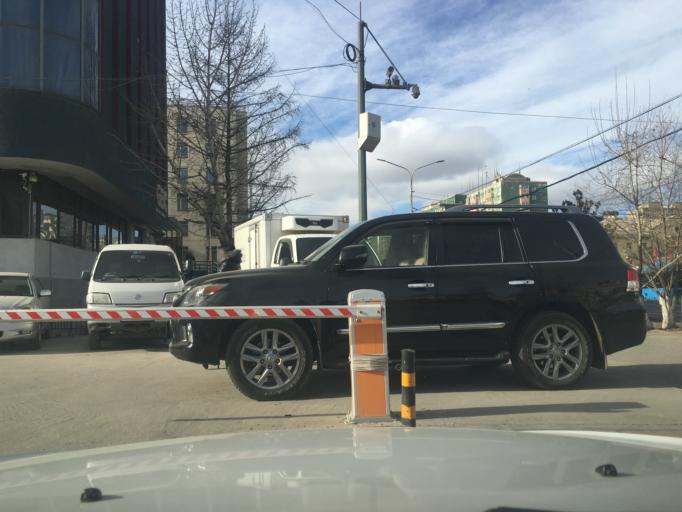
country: MN
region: Ulaanbaatar
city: Ulaanbaatar
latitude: 47.9144
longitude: 106.8813
